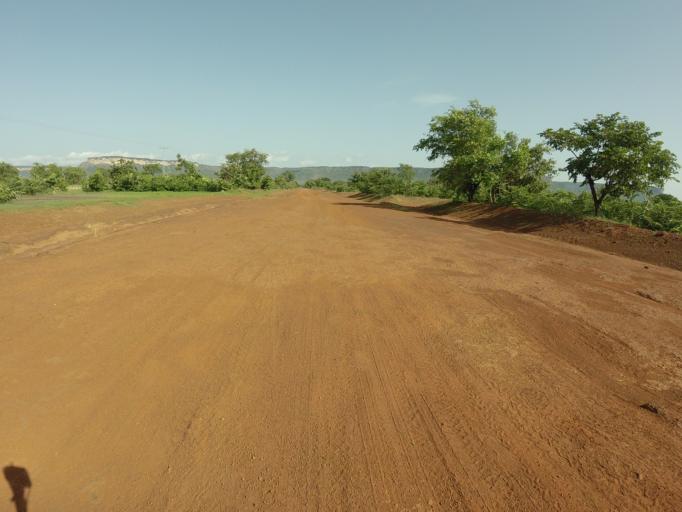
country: GH
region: Upper East
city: Bawku
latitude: 10.6832
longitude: -0.2147
